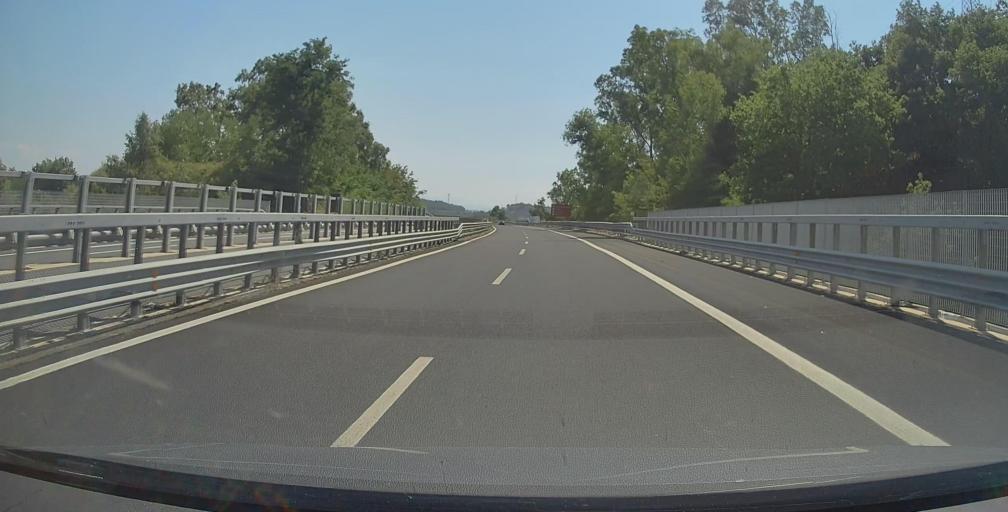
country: IT
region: Calabria
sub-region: Provincia di Reggio Calabria
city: Rosarno
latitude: 38.4954
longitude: 16.0125
